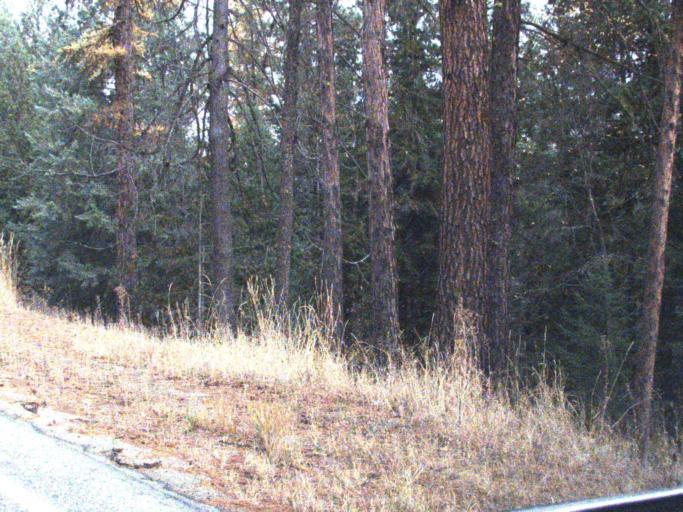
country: CA
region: British Columbia
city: Grand Forks
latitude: 48.8703
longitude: -118.2108
